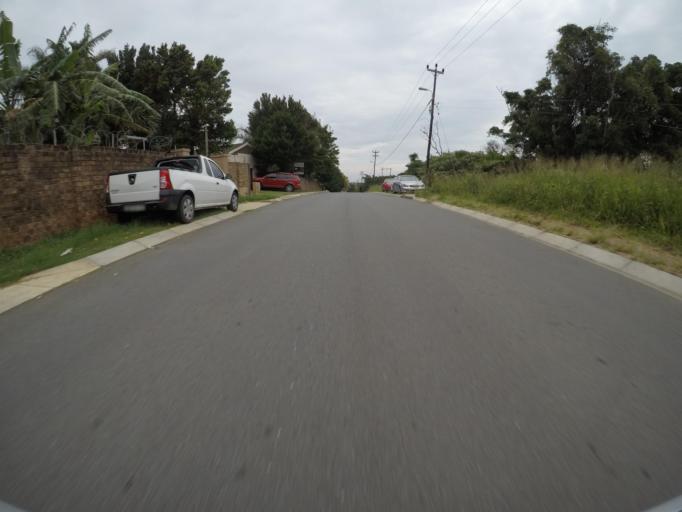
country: ZA
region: Eastern Cape
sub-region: Buffalo City Metropolitan Municipality
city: East London
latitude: -32.9370
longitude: 28.0029
